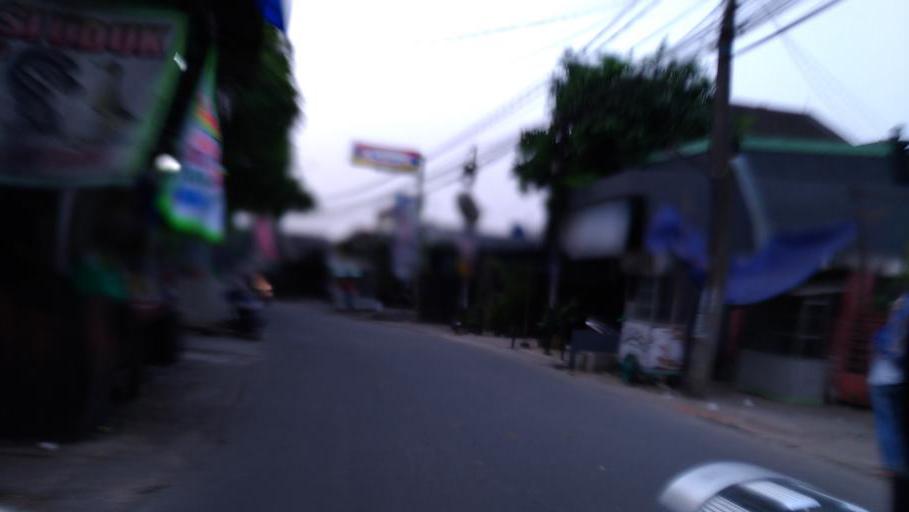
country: ID
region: West Java
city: Depok
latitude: -6.3618
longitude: 106.8694
